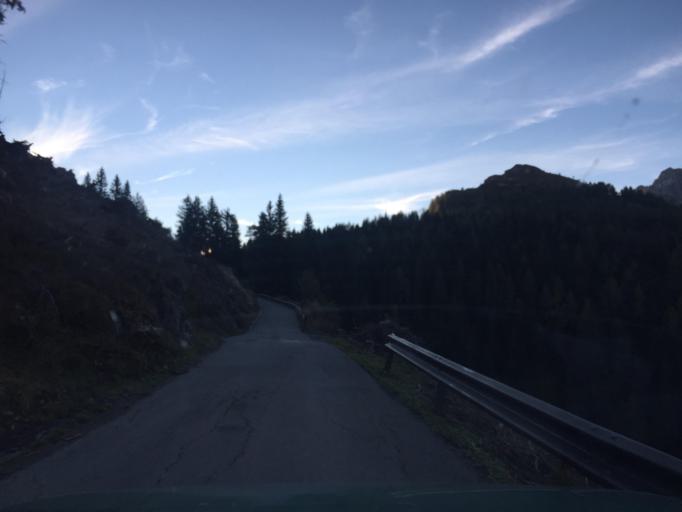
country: IT
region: Veneto
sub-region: Provincia di Belluno
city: Granvilla
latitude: 46.6140
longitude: 12.7208
